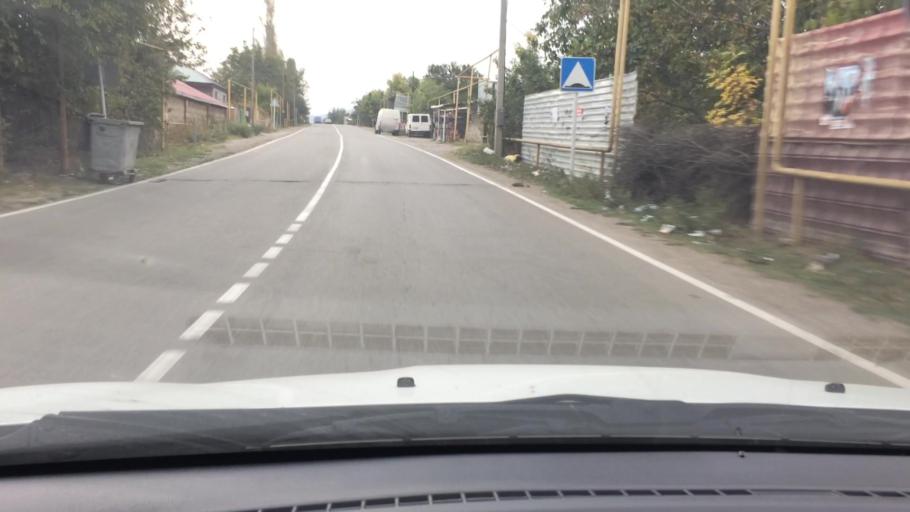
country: AM
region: Tavush
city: Bagratashen
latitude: 41.2375
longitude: 44.8038
